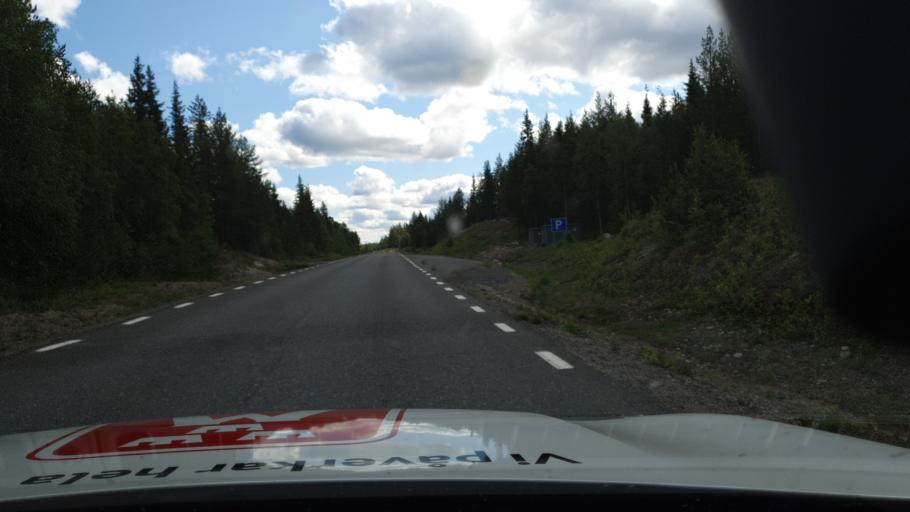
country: SE
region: Vaesterbotten
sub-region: Mala Kommun
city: Mala
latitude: 65.5279
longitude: 18.2466
